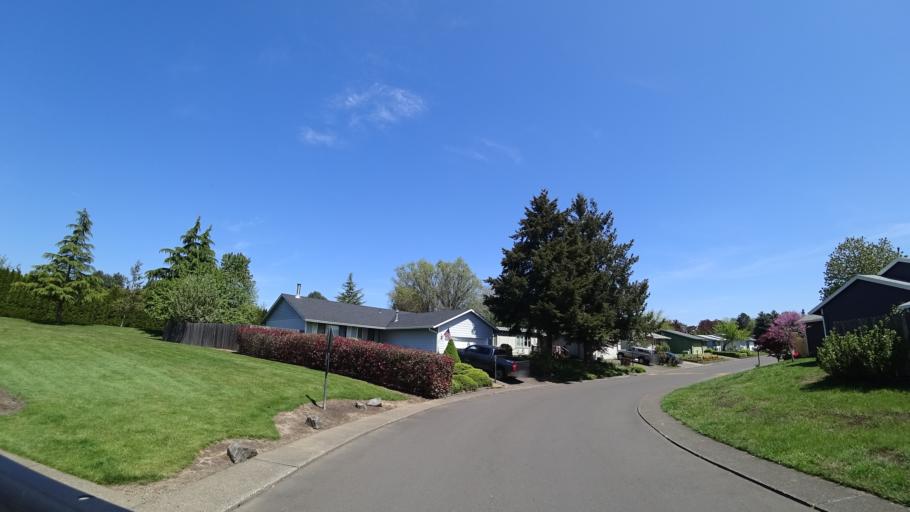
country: US
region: Oregon
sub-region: Washington County
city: Hillsboro
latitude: 45.5066
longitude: -122.9699
